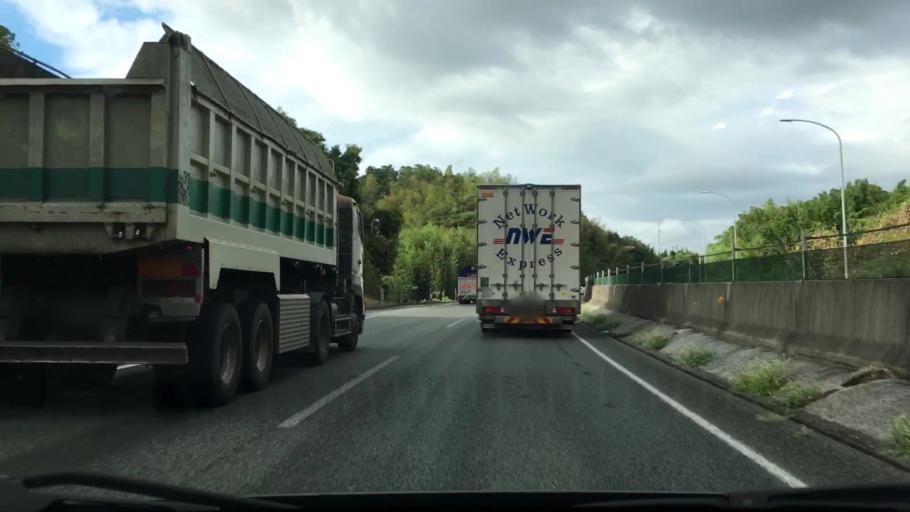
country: JP
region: Fukuoka
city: Nishifukuma
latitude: 33.7466
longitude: 130.5277
